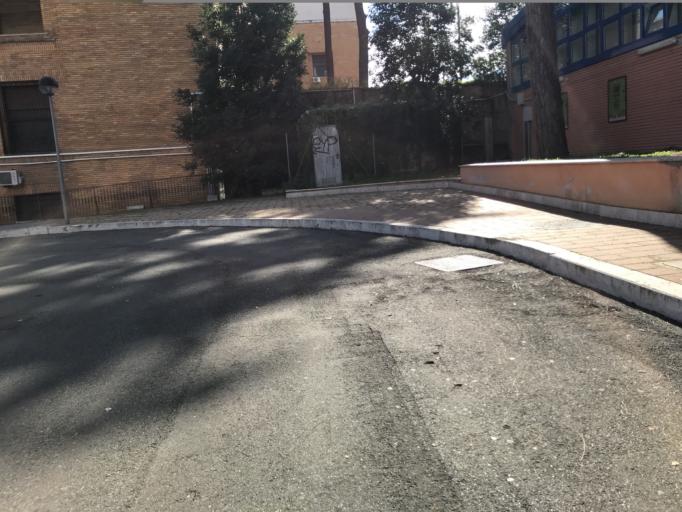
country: IT
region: Latium
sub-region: Citta metropolitana di Roma Capitale
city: Rome
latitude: 41.9032
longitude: 12.5119
